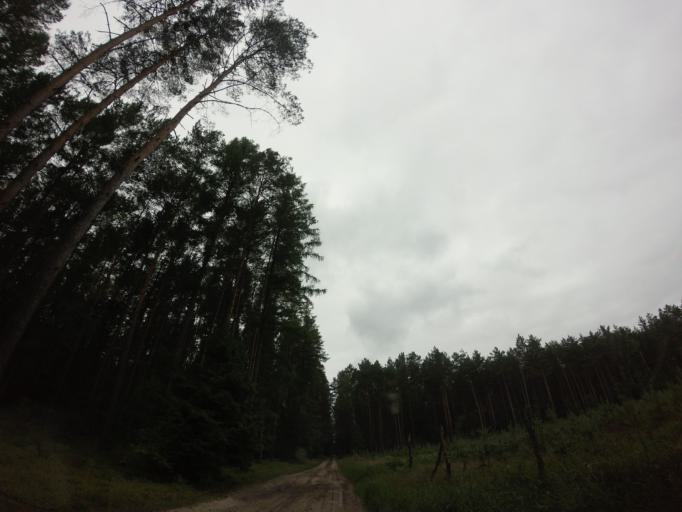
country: PL
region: Lubusz
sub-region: Powiat strzelecko-drezdenecki
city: Dobiegniew
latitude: 53.0923
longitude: 15.8443
